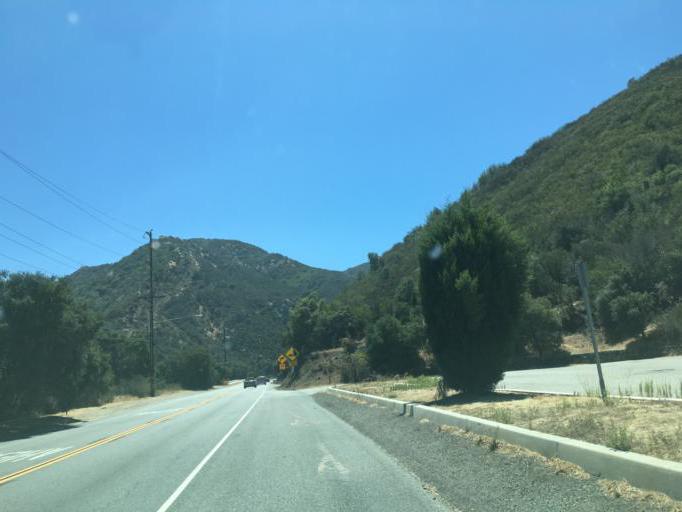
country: US
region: California
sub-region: Los Angeles County
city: Malibu Beach
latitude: 34.0802
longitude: -118.7037
